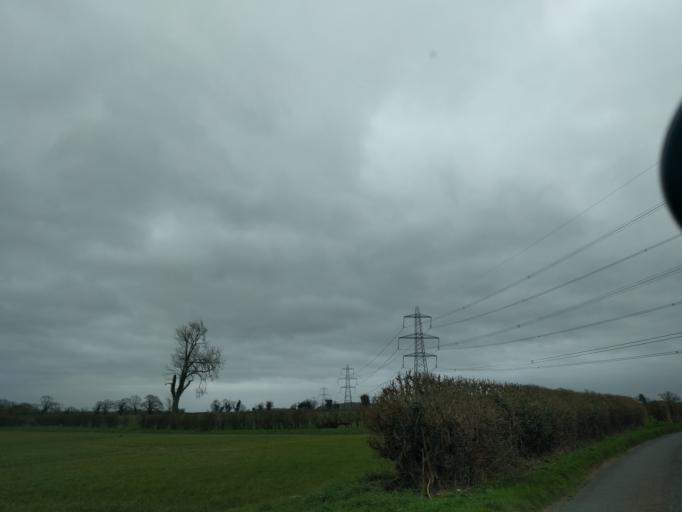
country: GB
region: England
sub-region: Wiltshire
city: Biddestone
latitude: 51.4773
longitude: -2.1958
